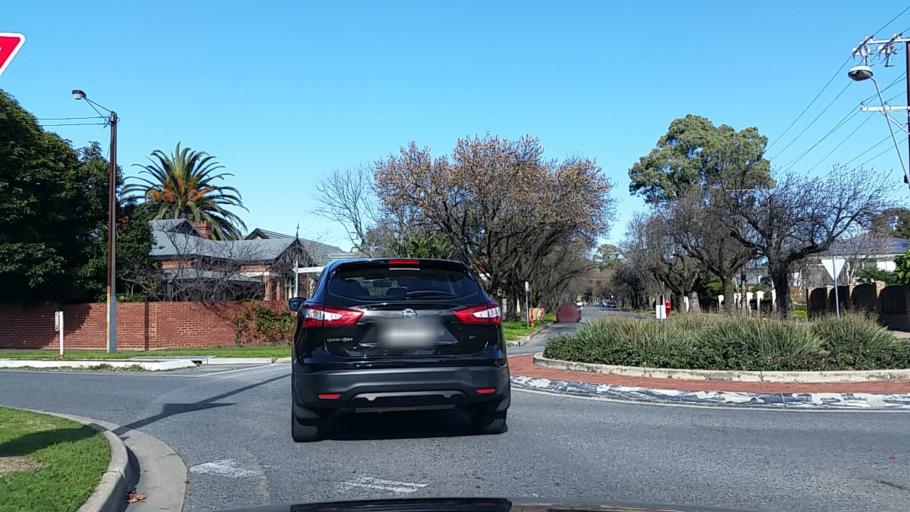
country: AU
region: South Australia
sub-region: Burnside
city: Tusmore
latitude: -34.9316
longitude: 138.6515
